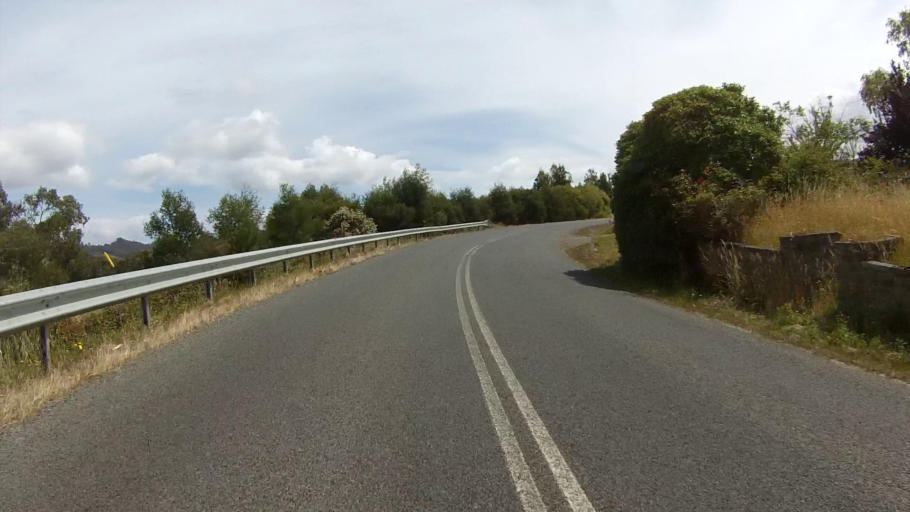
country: AU
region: Tasmania
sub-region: Huon Valley
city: Cygnet
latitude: -43.1900
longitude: 147.1008
